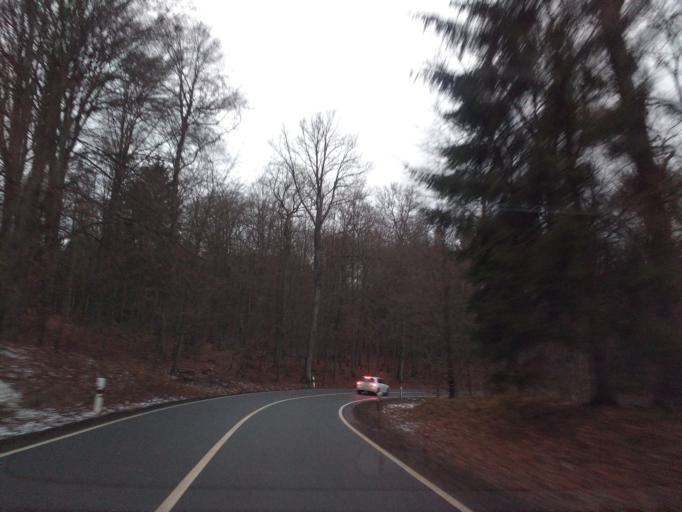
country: DE
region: Saxony-Anhalt
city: Neinstedt
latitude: 51.7115
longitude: 11.0807
